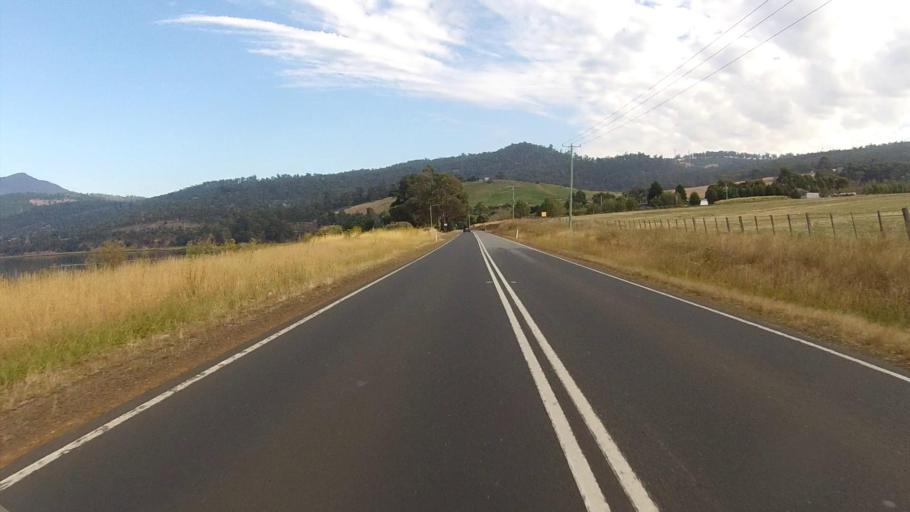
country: AU
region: Tasmania
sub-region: Brighton
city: Bridgewater
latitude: -42.7284
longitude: 147.2064
